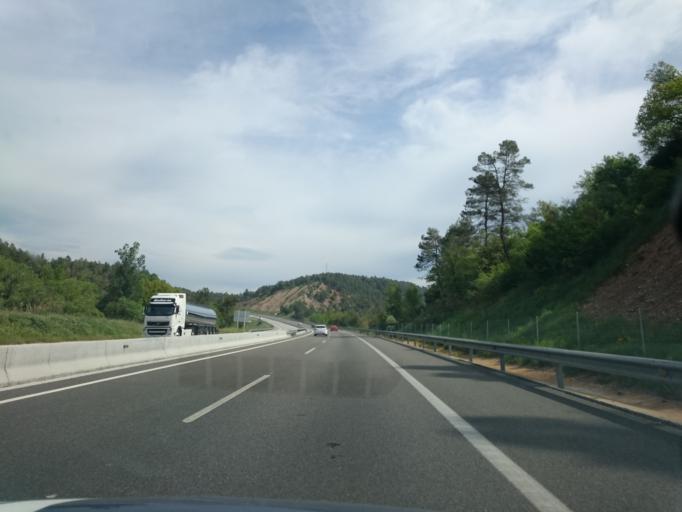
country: ES
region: Catalonia
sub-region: Provincia de Barcelona
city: Avinyo
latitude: 41.8387
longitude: 1.9808
